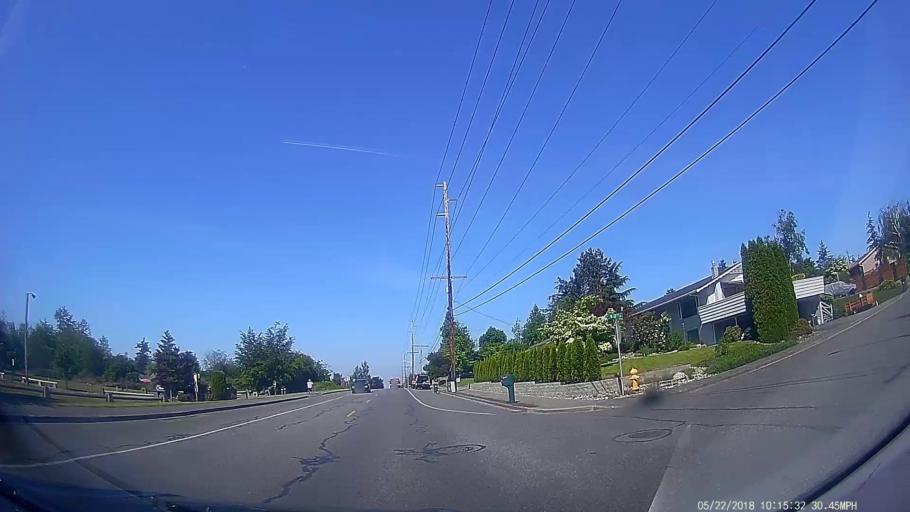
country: US
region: Washington
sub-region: Skagit County
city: Mount Vernon
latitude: 48.4429
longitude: -122.3059
